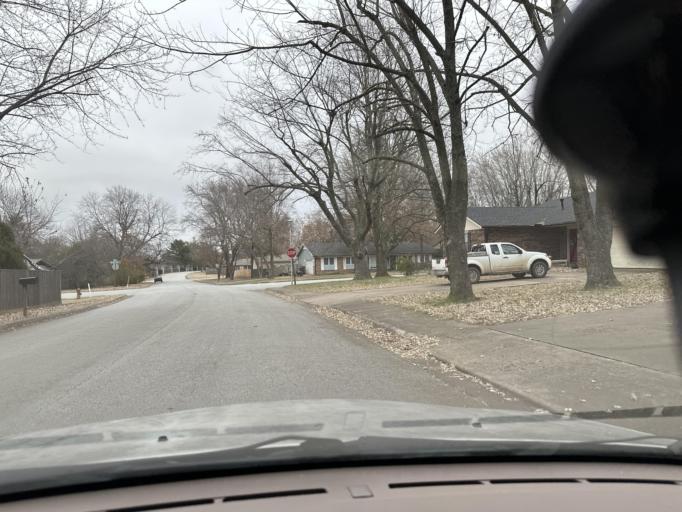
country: US
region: Arkansas
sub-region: Washington County
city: Fayetteville
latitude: 36.0854
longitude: -94.1159
